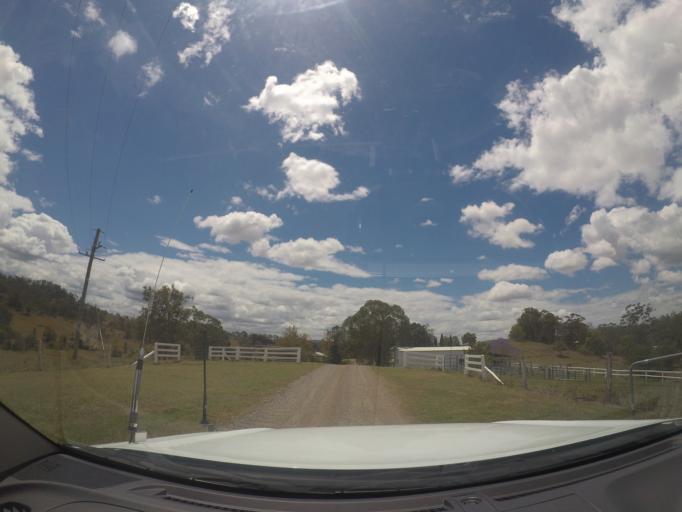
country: AU
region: Queensland
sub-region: Logan
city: Cedar Vale
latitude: -27.9059
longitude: 153.0576
